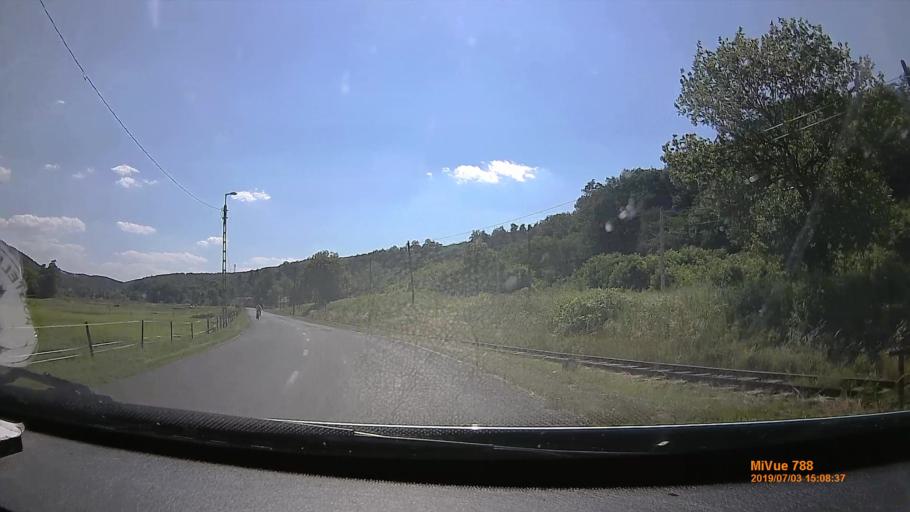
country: HU
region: Borsod-Abauj-Zemplen
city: Putnok
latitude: 48.2436
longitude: 20.3791
